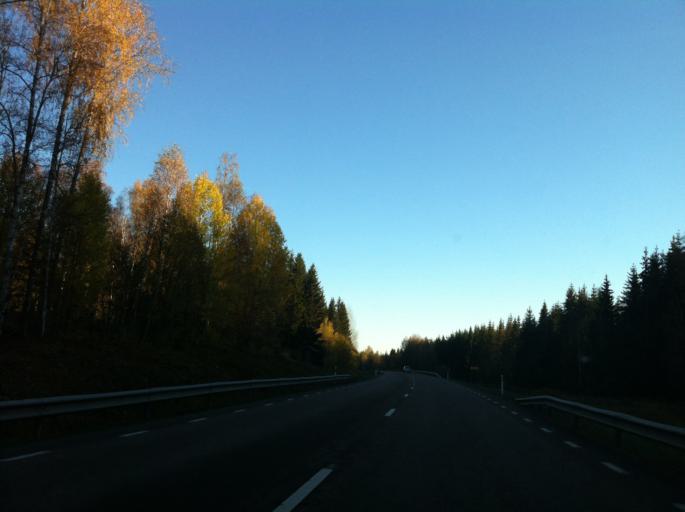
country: SE
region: Dalarna
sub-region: Faluns Kommun
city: Falun
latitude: 60.6539
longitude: 15.5565
